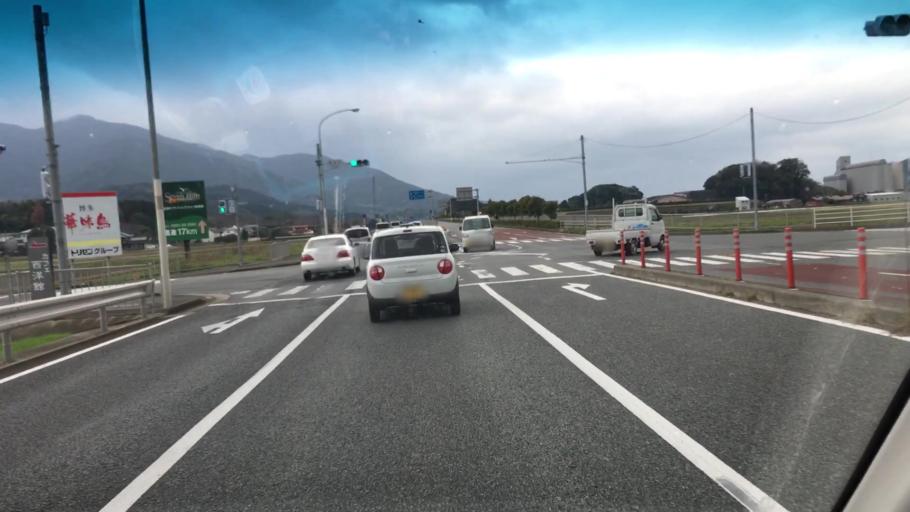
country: JP
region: Fukuoka
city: Maebaru-chuo
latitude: 33.5223
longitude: 130.1673
